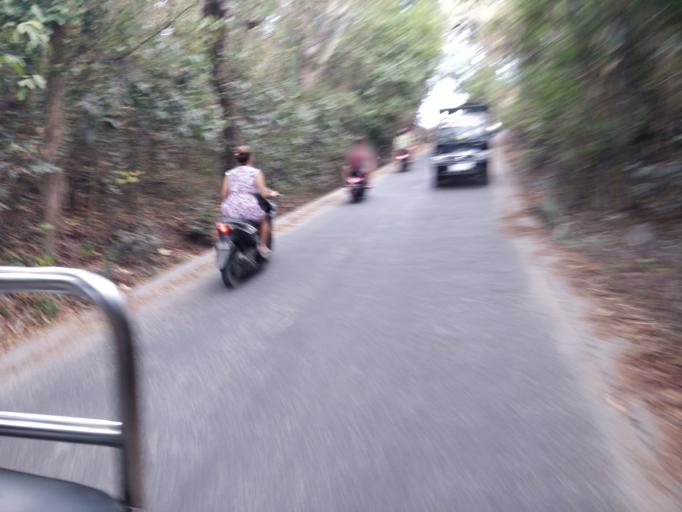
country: ID
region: Bali
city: Jungutbatu Kaja Dua
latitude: -8.6812
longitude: 115.4475
